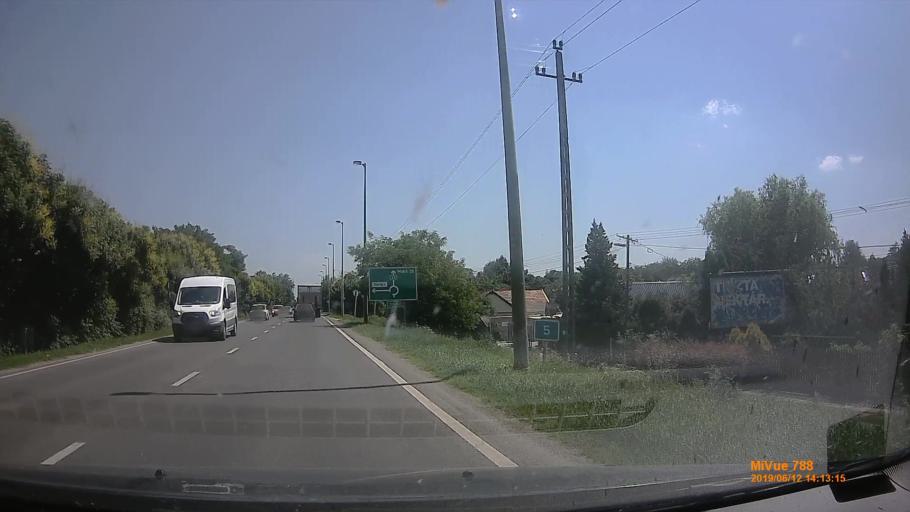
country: HU
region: Csongrad
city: Szeged
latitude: 46.2339
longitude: 20.1730
